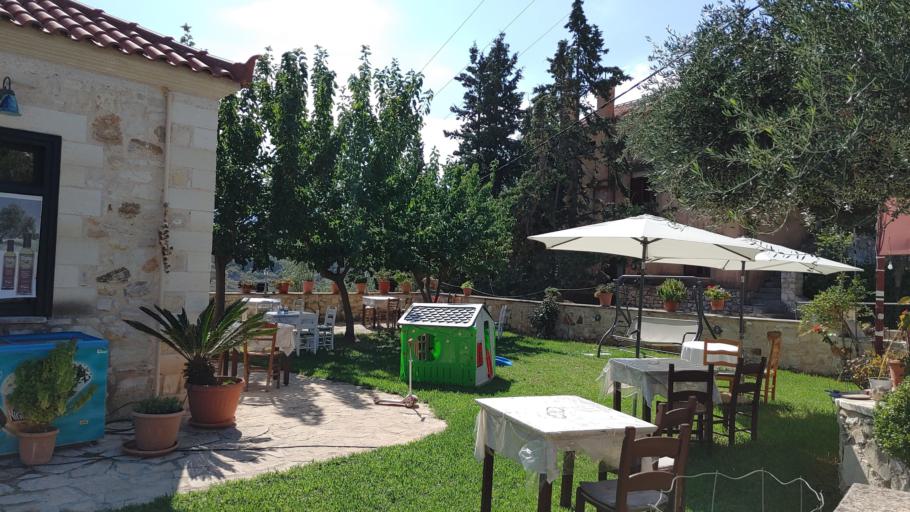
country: GR
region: Crete
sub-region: Nomos Chanias
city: Kalivai
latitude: 35.4276
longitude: 24.1908
